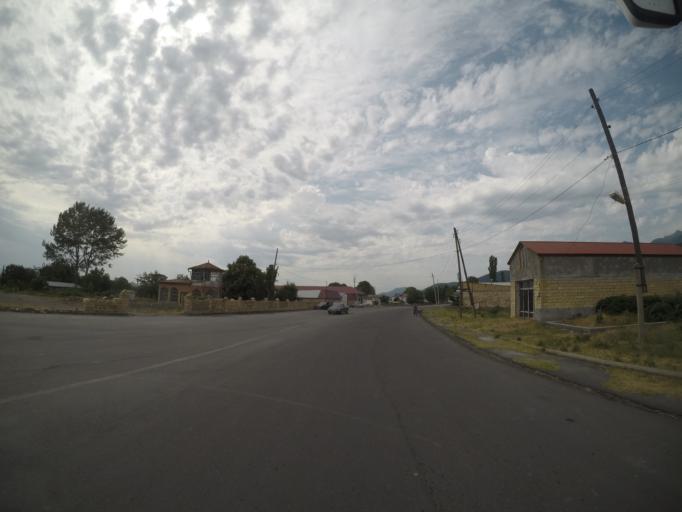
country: AZ
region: Qakh Rayon
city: Qax
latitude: 41.4151
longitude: 46.9077
